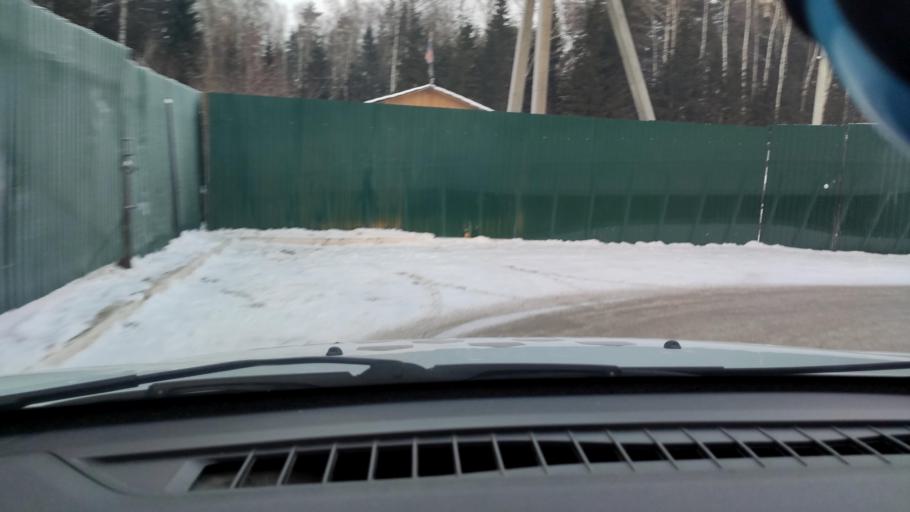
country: RU
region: Perm
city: Kondratovo
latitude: 58.0487
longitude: 56.0823
